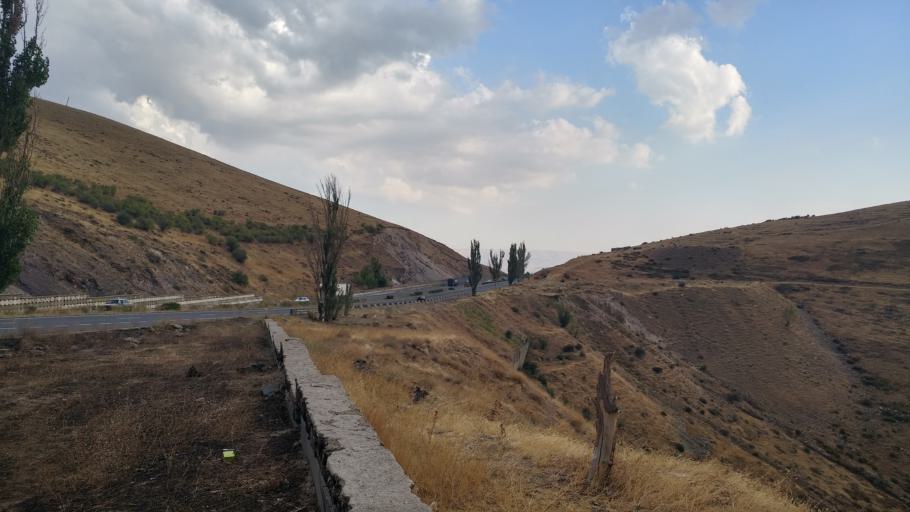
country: AM
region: Kotayk'i Marz
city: Argel
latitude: 40.3525
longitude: 44.6296
